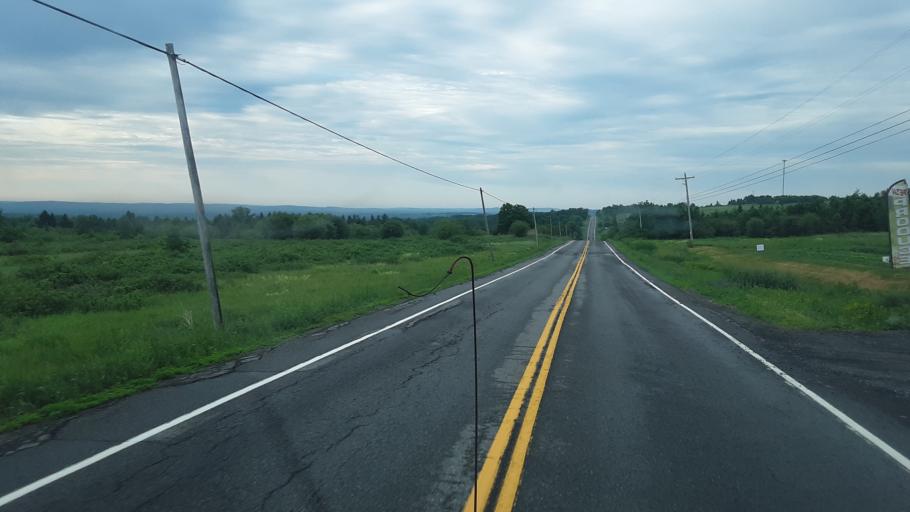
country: US
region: Maine
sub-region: Penobscot County
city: Patten
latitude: 46.0414
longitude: -68.4439
